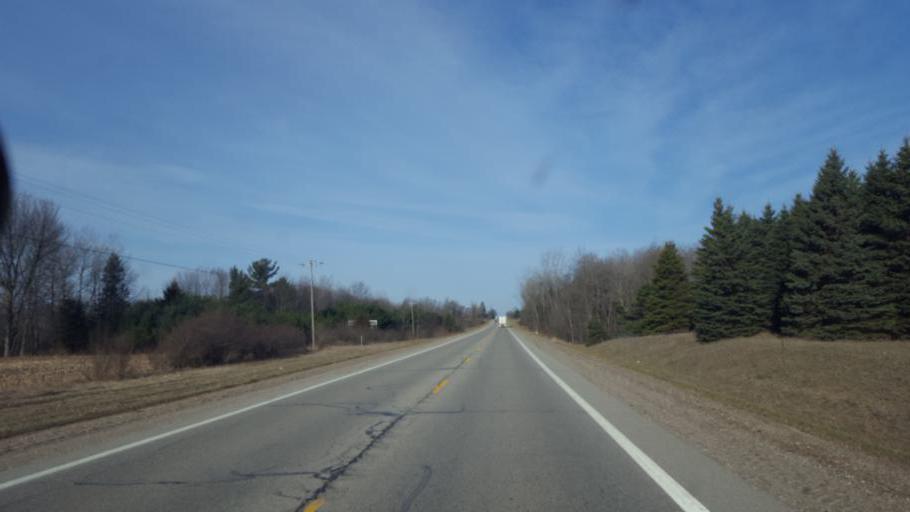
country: US
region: Michigan
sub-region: Montcalm County
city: Lakeview
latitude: 43.4301
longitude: -85.1673
